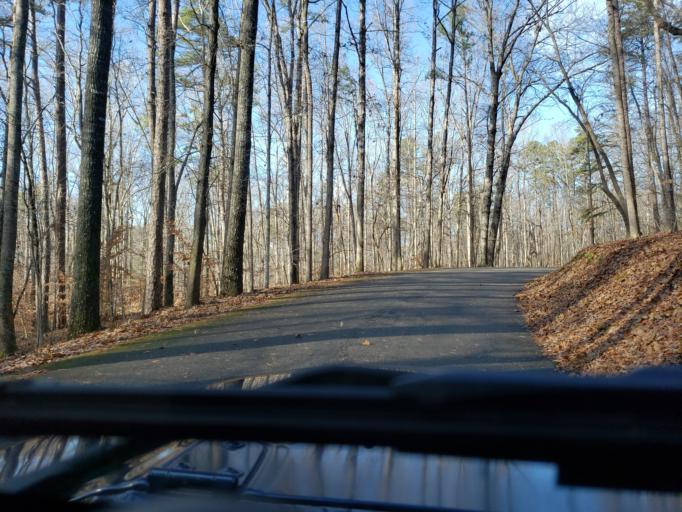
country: US
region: North Carolina
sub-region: Cleveland County
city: Kings Mountain
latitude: 35.1505
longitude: -81.3359
